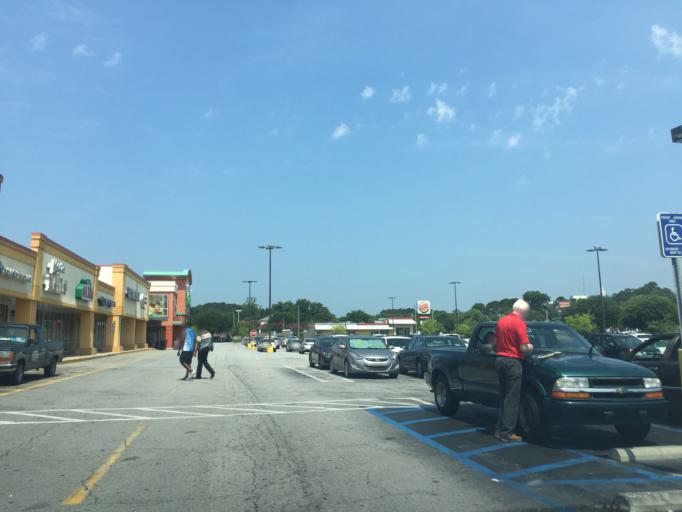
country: US
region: Georgia
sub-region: Chatham County
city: Montgomery
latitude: 31.9814
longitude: -81.1510
